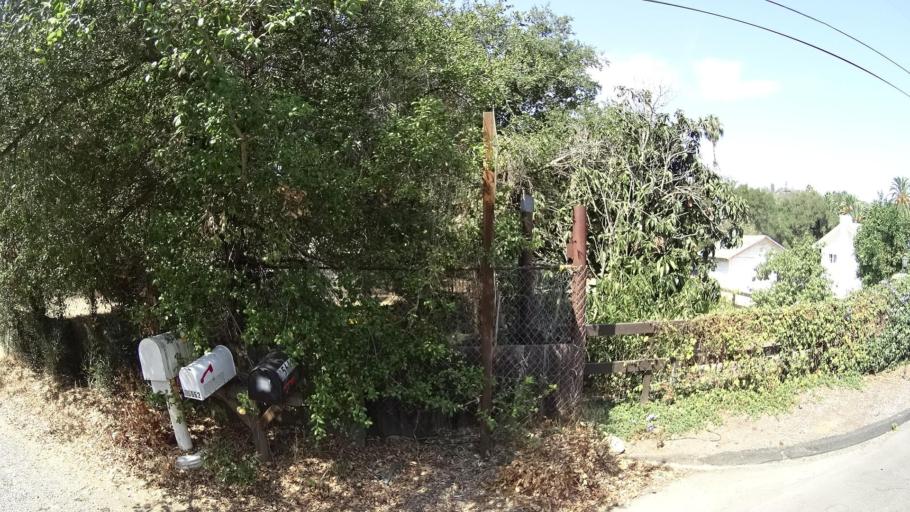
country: US
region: California
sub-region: San Diego County
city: Hidden Meadows
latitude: 33.1783
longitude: -117.1085
